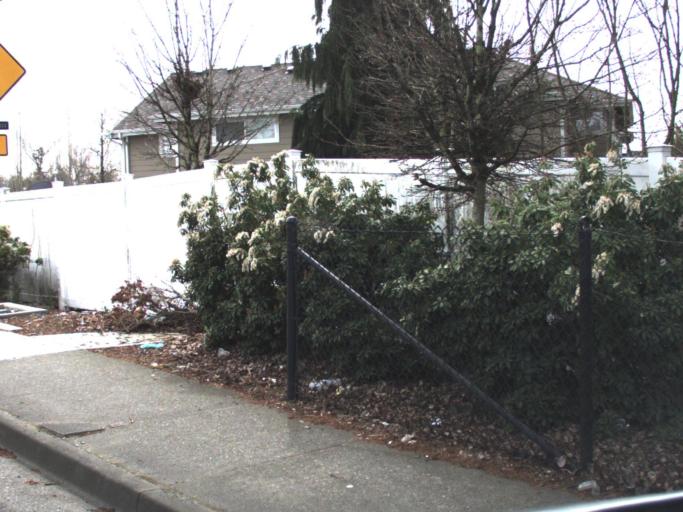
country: US
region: Washington
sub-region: King County
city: Kent
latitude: 47.3714
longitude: -122.1989
